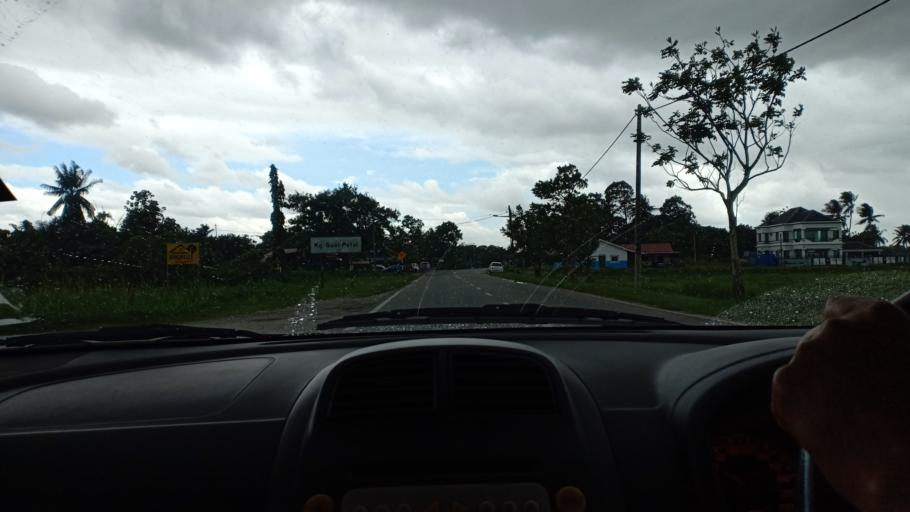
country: MY
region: Penang
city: Tasek Glugor
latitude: 5.4434
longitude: 100.4730
